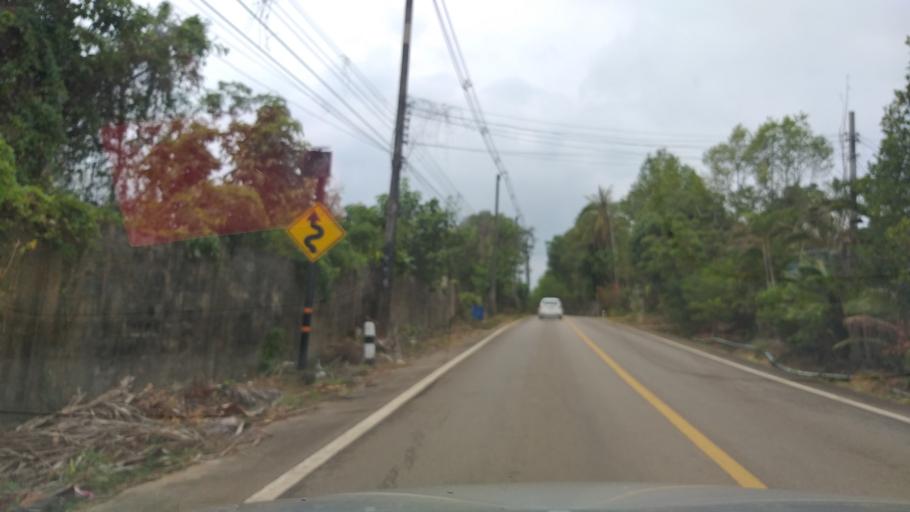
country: TH
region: Trat
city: Laem Ngop
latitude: 12.1933
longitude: 102.2905
